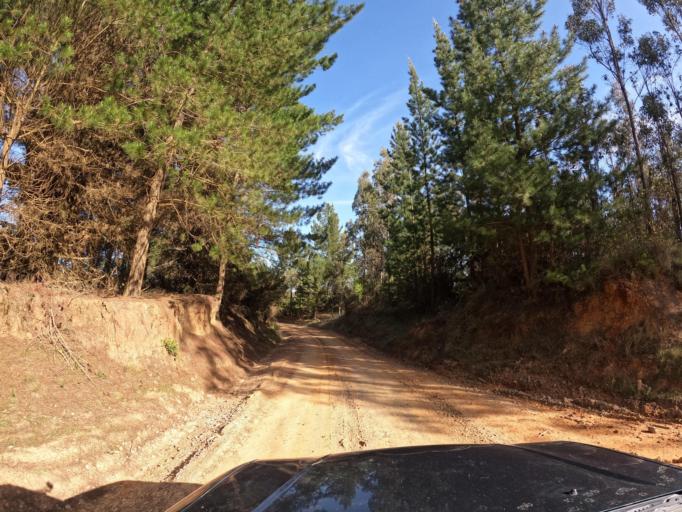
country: CL
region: Biobio
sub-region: Provincia de Biobio
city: La Laja
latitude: -37.1162
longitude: -72.7391
